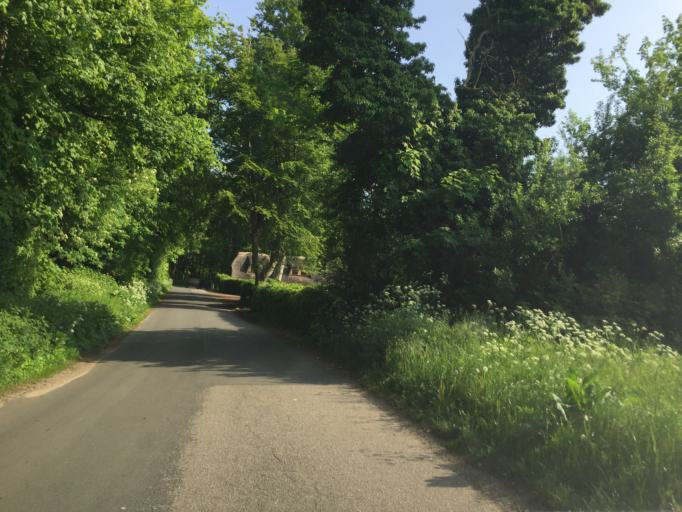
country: DK
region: South Denmark
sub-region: Svendborg Kommune
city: Thuro By
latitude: 55.1292
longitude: 10.7774
